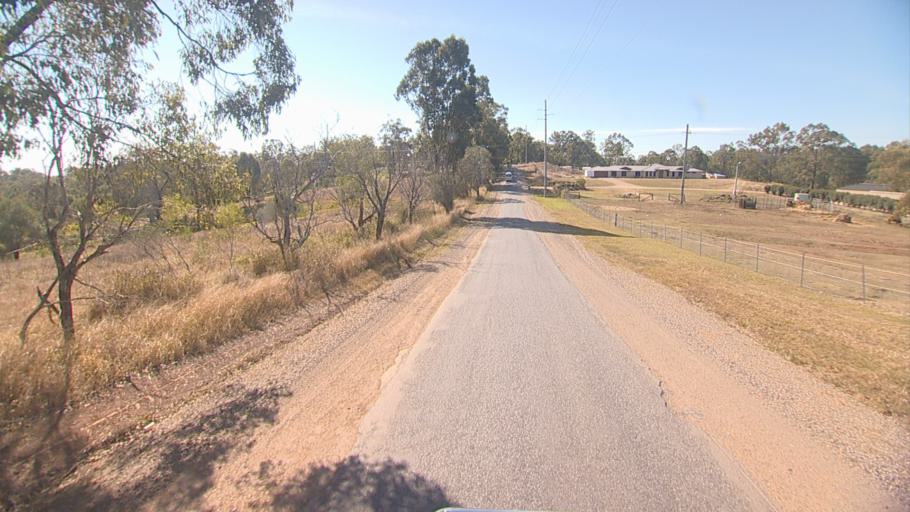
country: AU
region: Queensland
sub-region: Logan
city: Cedar Vale
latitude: -27.8947
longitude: 153.0157
